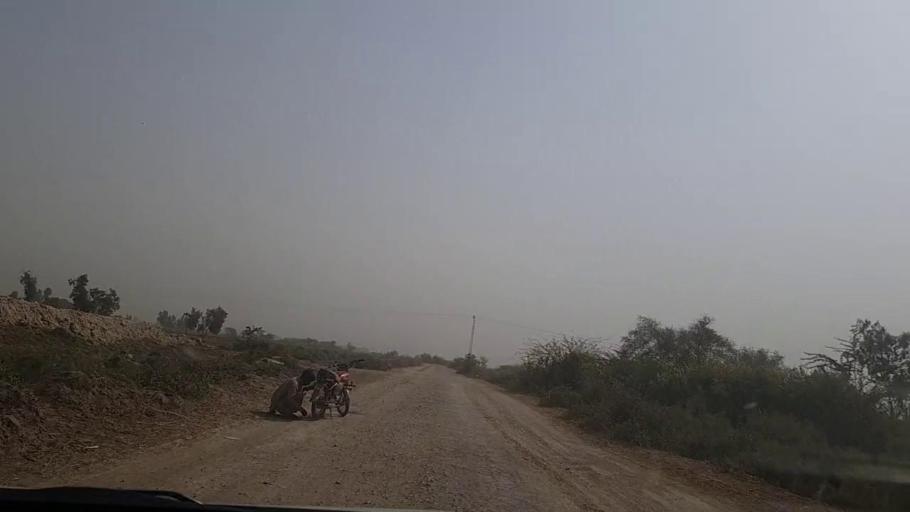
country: PK
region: Sindh
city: Pithoro
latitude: 25.4648
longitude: 69.2276
